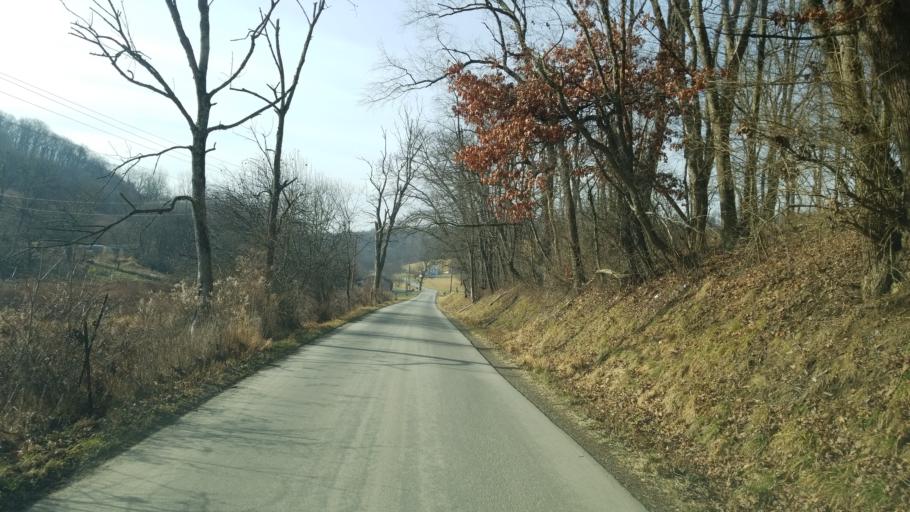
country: US
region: Pennsylvania
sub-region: Indiana County
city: Chevy Chase Heights
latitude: 40.8100
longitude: -79.1621
